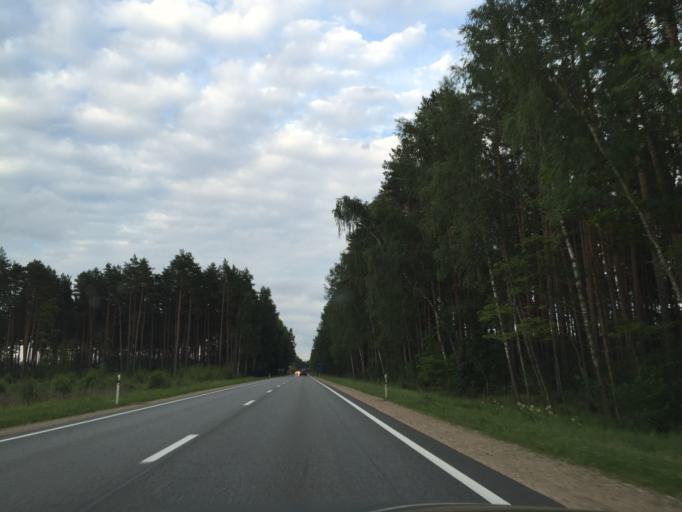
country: LV
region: Babite
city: Pinki
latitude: 56.9222
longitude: 23.8994
